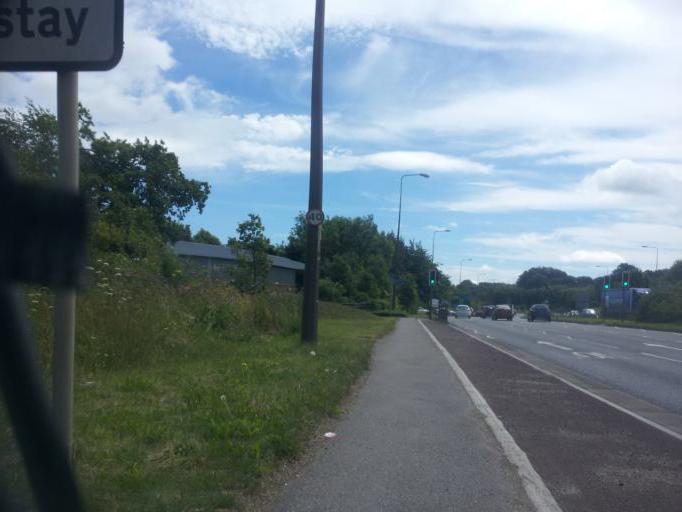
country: GB
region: England
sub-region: Kent
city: Aylesford
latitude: 51.3367
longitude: 0.5053
